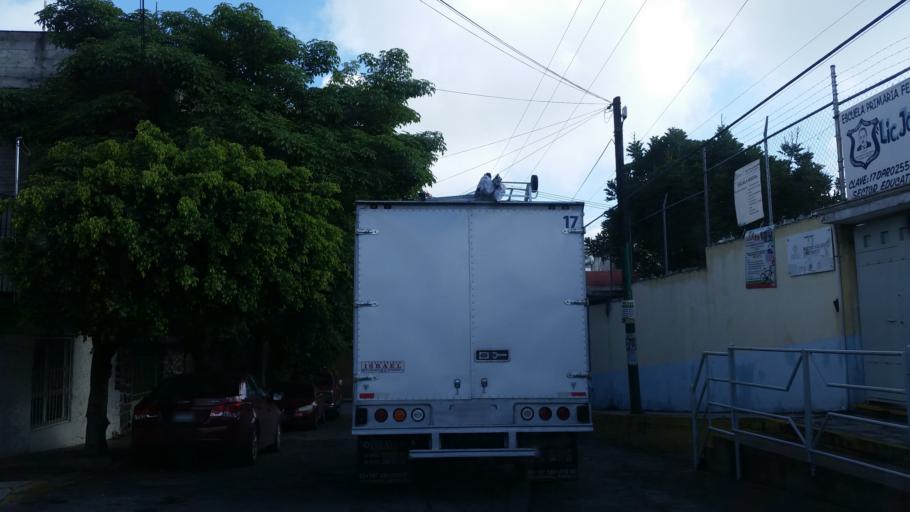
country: MX
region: Morelos
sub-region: Cuernavaca
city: Cuernavaca
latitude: 18.9188
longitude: -99.2077
